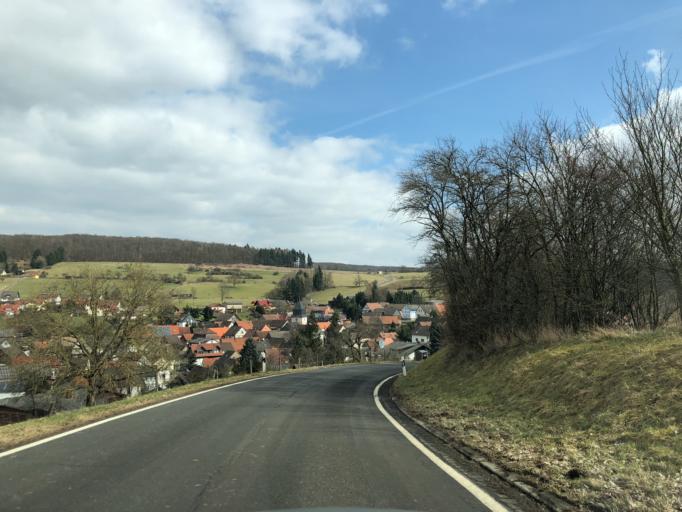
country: DE
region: Hesse
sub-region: Regierungsbezirk Giessen
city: Schotten
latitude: 50.5007
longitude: 9.0681
